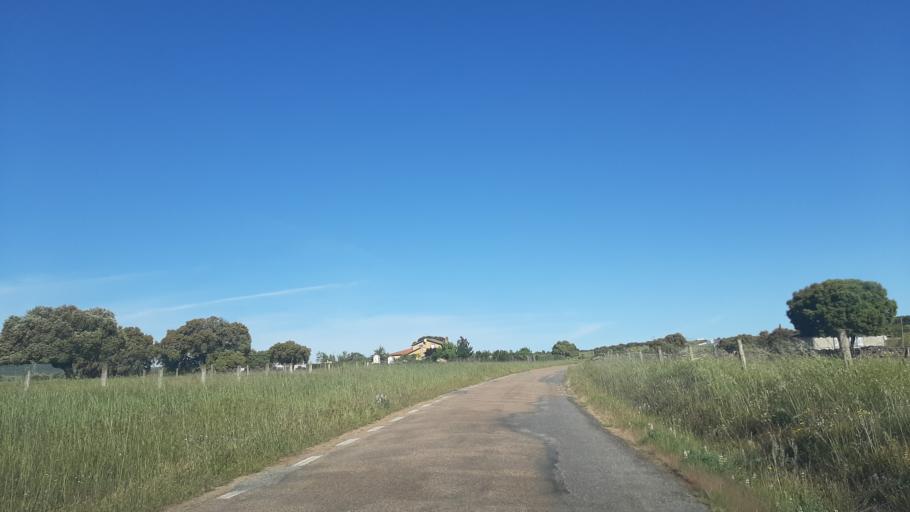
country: ES
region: Castille and Leon
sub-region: Provincia de Salamanca
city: Guijo de Avila
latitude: 40.5373
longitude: -5.6558
